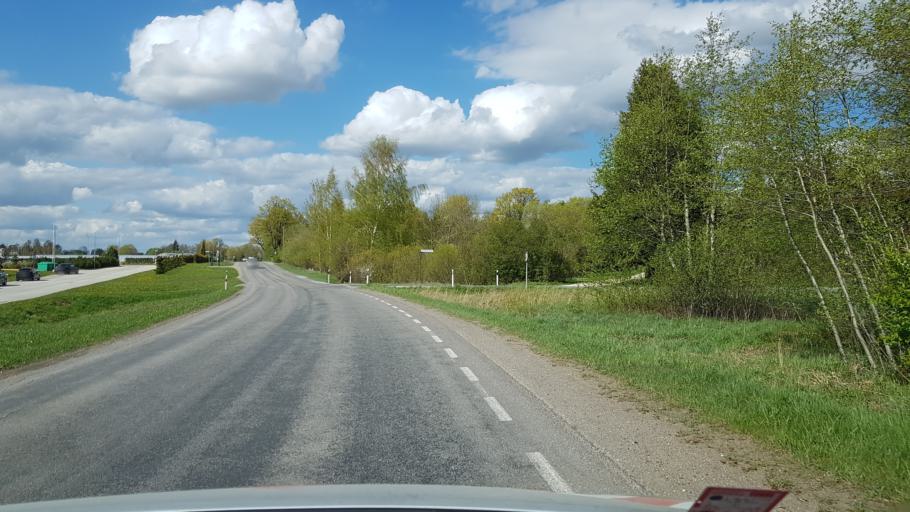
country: EE
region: Tartu
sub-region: Tartu linn
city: Tartu
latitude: 58.3646
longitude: 26.7988
